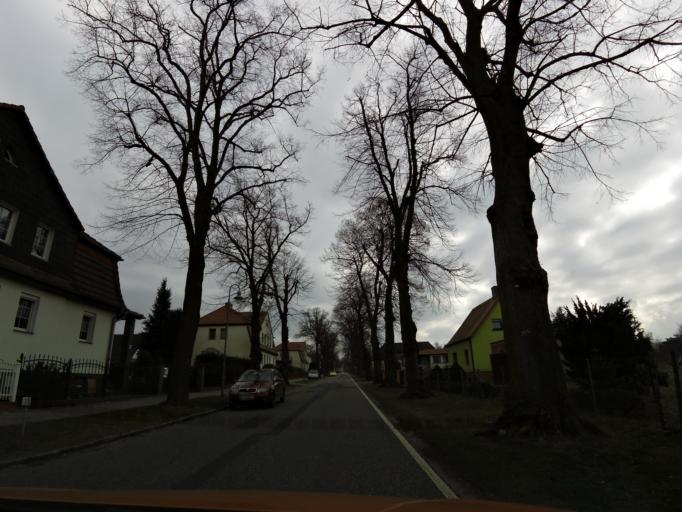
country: DE
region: Brandenburg
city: Ketzin
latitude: 52.4717
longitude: 12.8554
